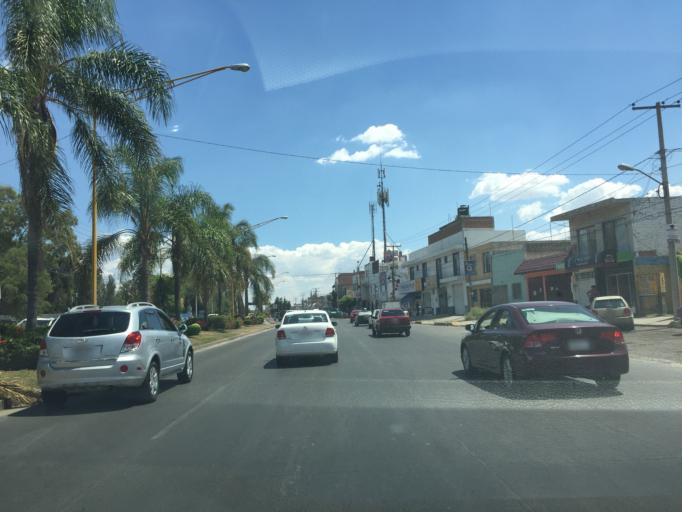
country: MX
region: Aguascalientes
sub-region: Aguascalientes
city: La Loma de los Negritos
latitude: 21.8542
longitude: -102.3172
